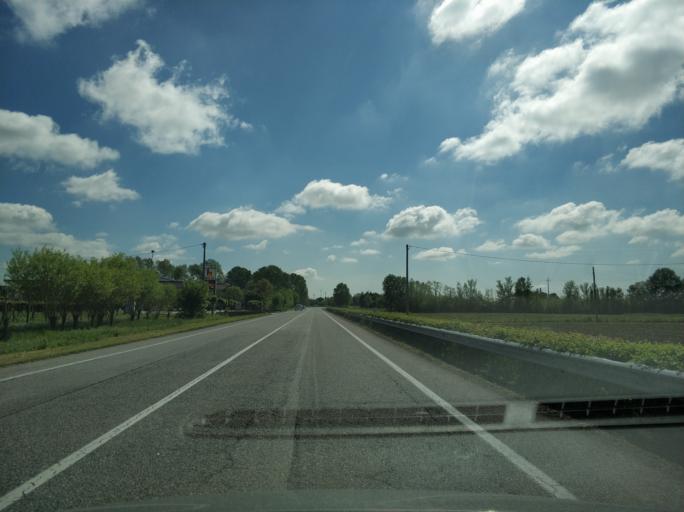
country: IT
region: Veneto
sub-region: Provincia di Venezia
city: Arino
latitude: 45.4320
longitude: 12.0460
